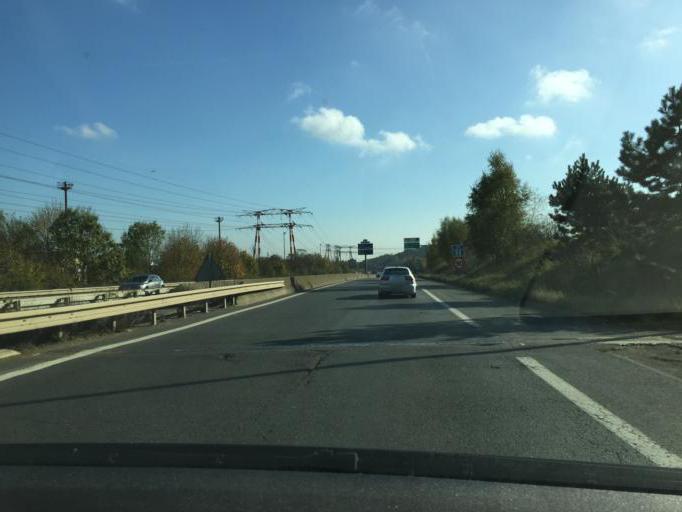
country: FR
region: Ile-de-France
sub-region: Departement de l'Essonne
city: Palaiseau
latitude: 48.7197
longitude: 2.2562
